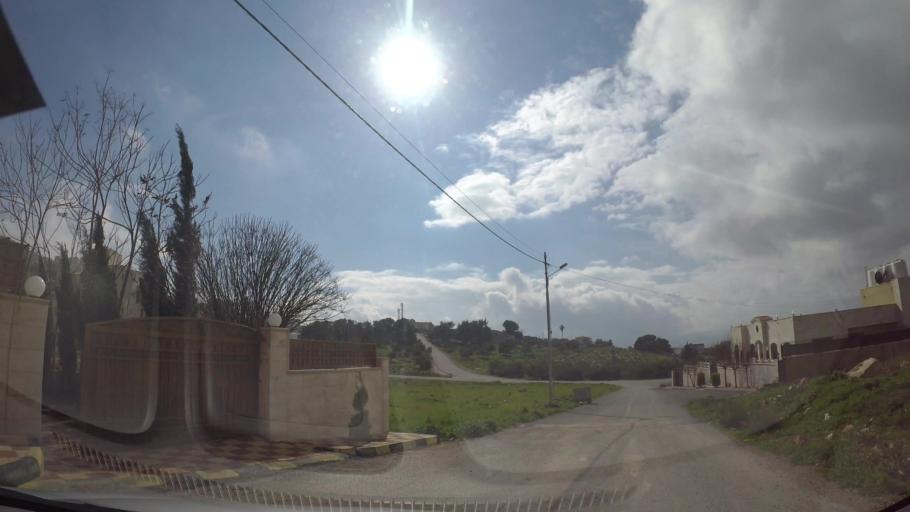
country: JO
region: Amman
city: Al Jubayhah
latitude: 32.0697
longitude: 35.8717
